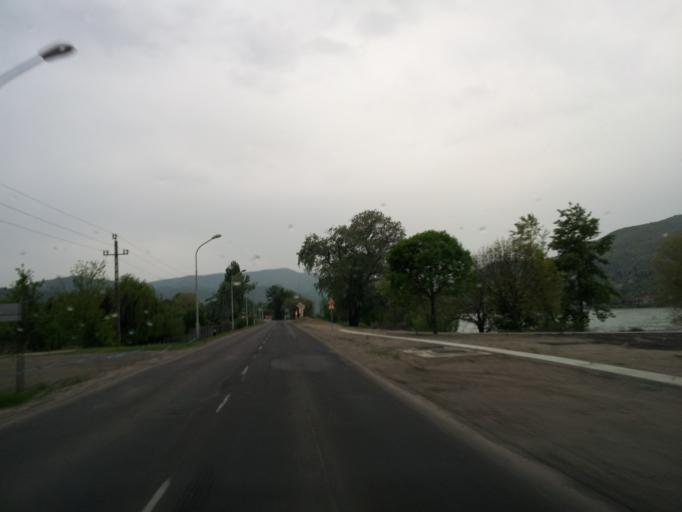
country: HU
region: Pest
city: Visegrad
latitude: 47.7899
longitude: 18.9704
